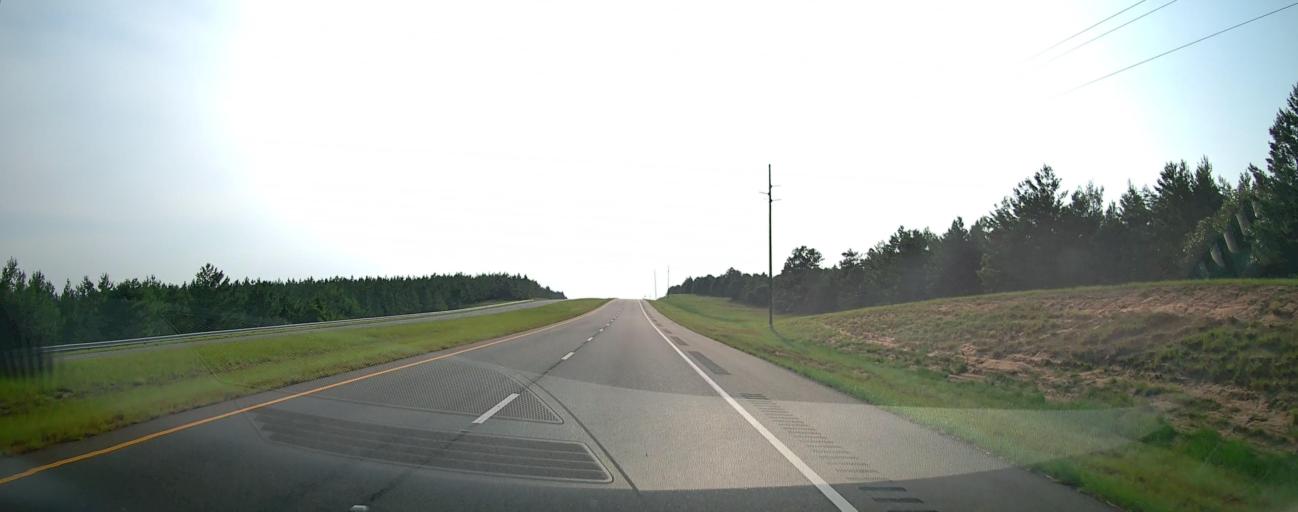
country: US
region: Georgia
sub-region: Talbot County
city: Talbotton
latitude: 32.5947
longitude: -84.4181
